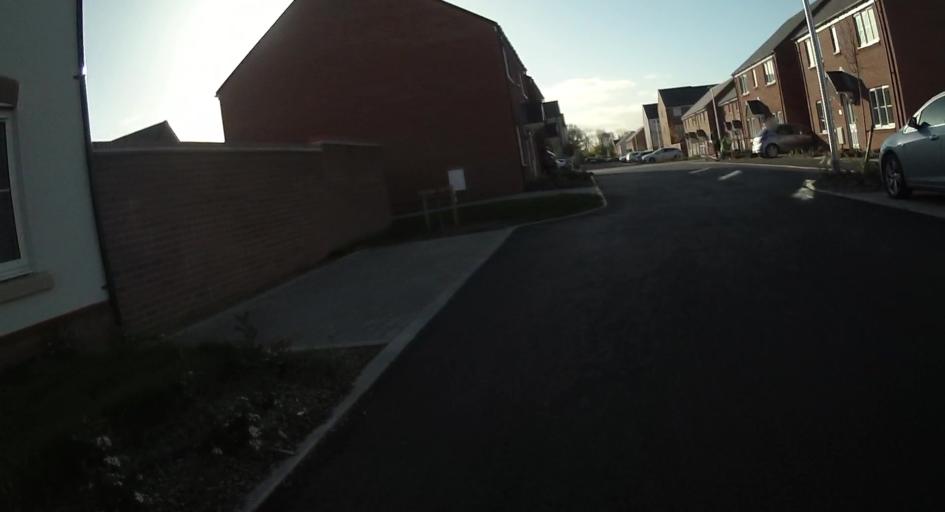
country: GB
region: England
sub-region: Wokingham
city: Winnersh
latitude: 51.4283
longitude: -0.8874
